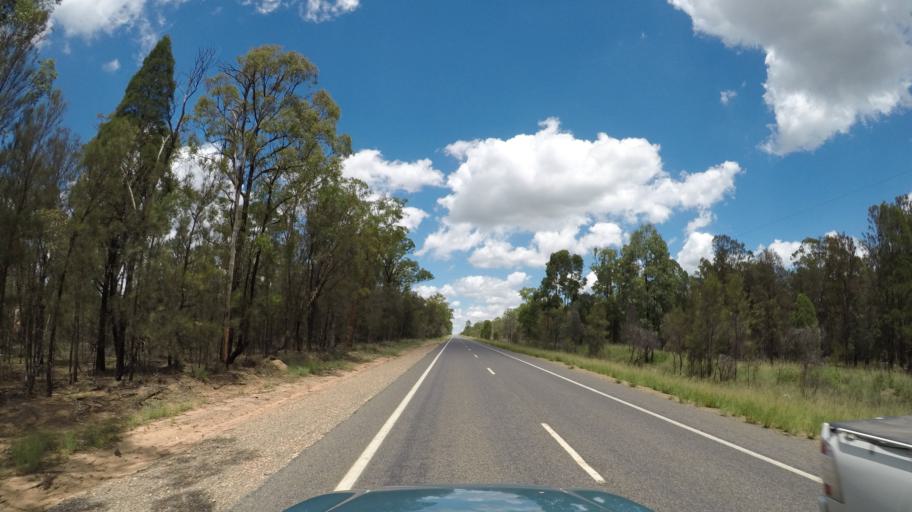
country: AU
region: Queensland
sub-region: Goondiwindi
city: Goondiwindi
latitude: -27.9970
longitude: 150.9464
